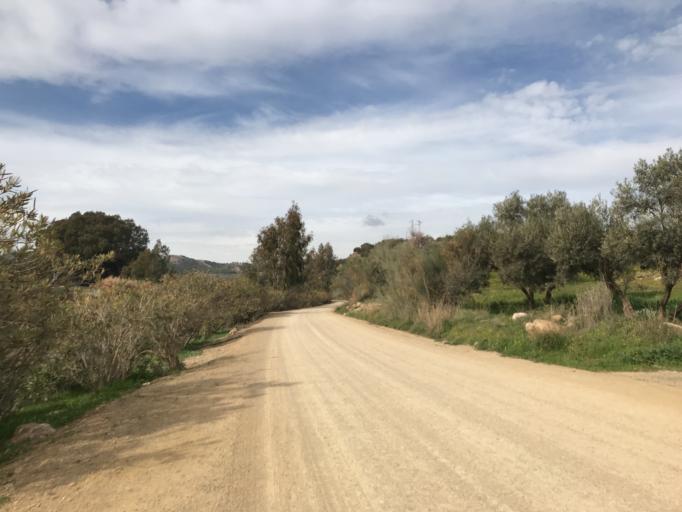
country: ES
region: Andalusia
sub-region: Provincia de Malaga
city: Ardales
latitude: 36.8826
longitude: -4.8535
